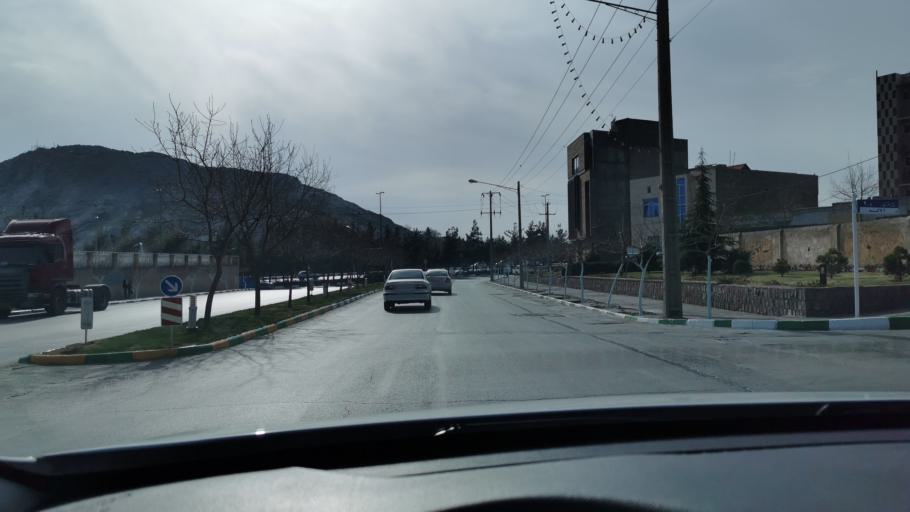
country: IR
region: Razavi Khorasan
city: Mashhad
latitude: 36.2806
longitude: 59.5542
